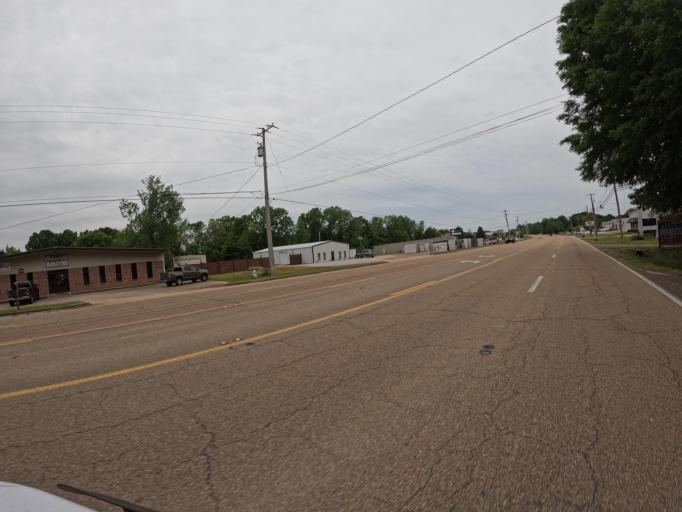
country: US
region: Mississippi
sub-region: Lee County
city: Tupelo
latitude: 34.2891
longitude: -88.7456
